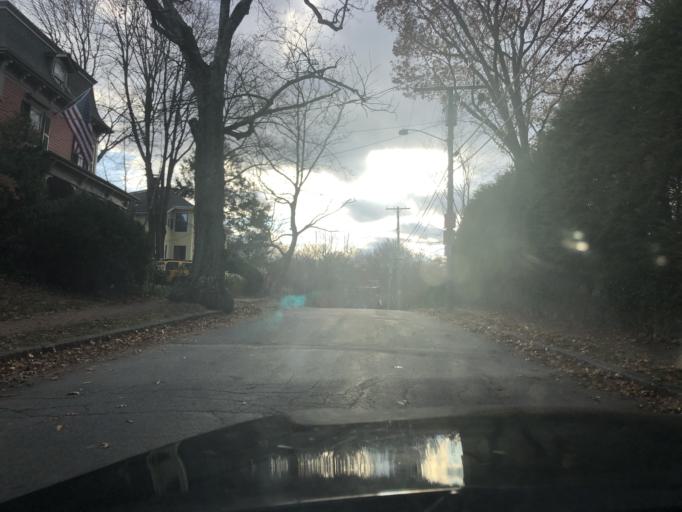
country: US
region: Massachusetts
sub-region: Middlesex County
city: Arlington
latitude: 42.4138
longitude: -71.1585
